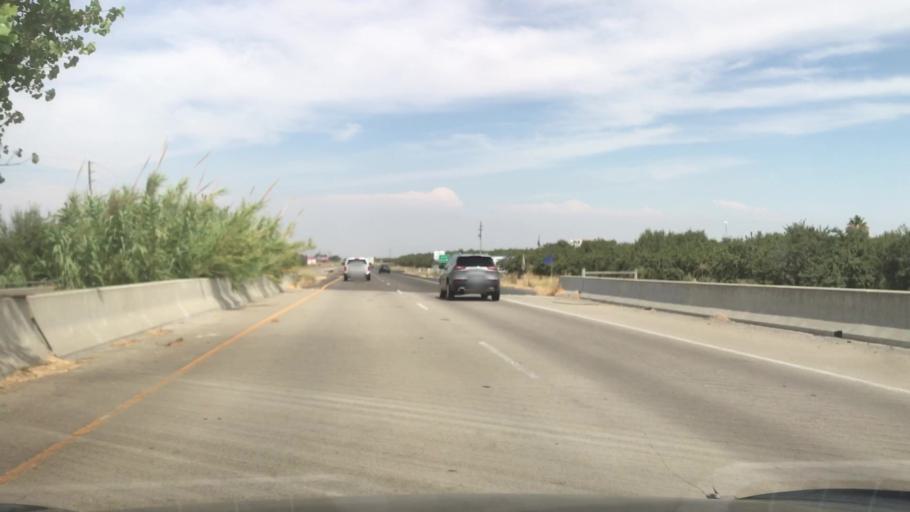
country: US
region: California
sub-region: Madera County
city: Chowchilla
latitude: 37.0836
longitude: -120.2684
